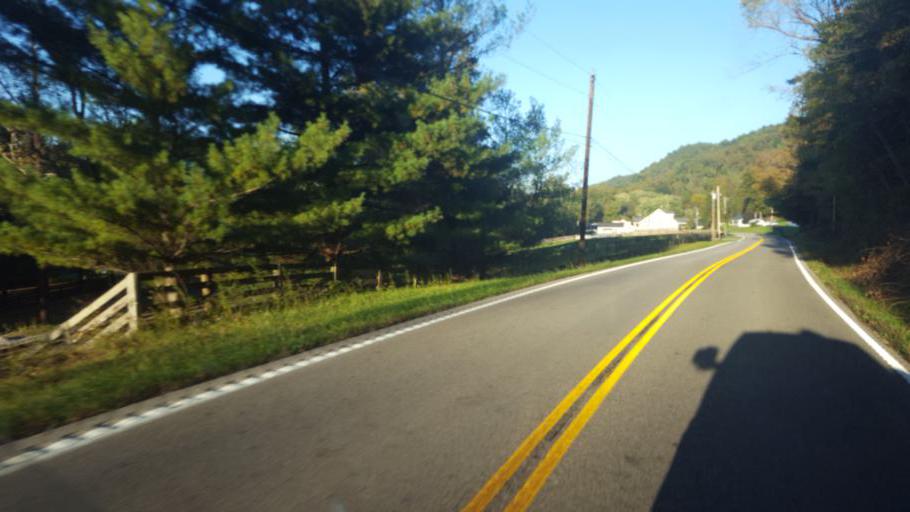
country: US
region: Ohio
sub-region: Scioto County
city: West Portsmouth
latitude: 38.6820
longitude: -83.0694
